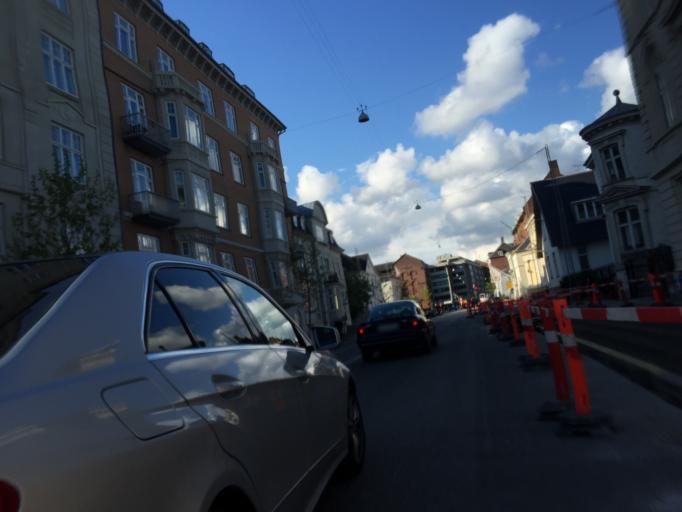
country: DK
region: Capital Region
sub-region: Frederiksberg Kommune
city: Frederiksberg
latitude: 55.6737
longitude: 12.5440
